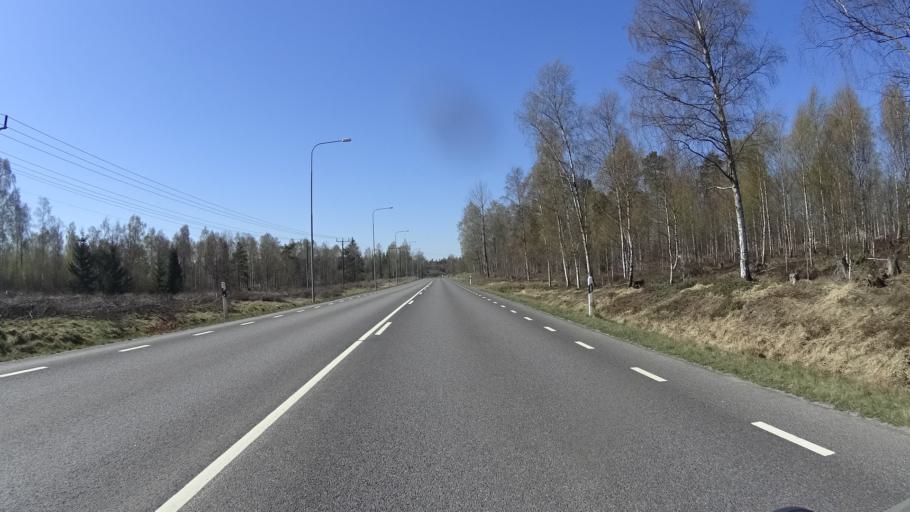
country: SE
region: Kronoberg
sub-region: Ljungby Kommun
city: Ljungby
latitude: 56.8305
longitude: 13.9739
